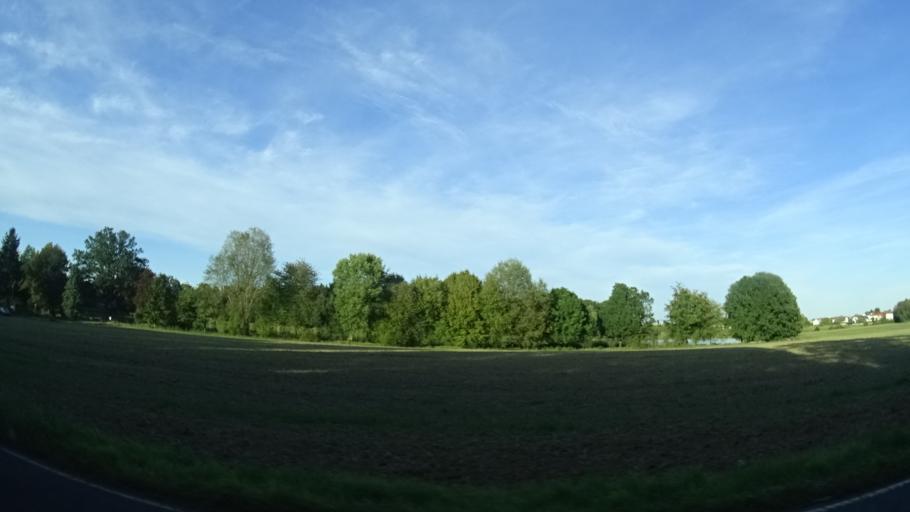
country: DE
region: Hesse
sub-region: Regierungsbezirk Darmstadt
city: Wachtersbach
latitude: 50.2875
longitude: 9.2514
